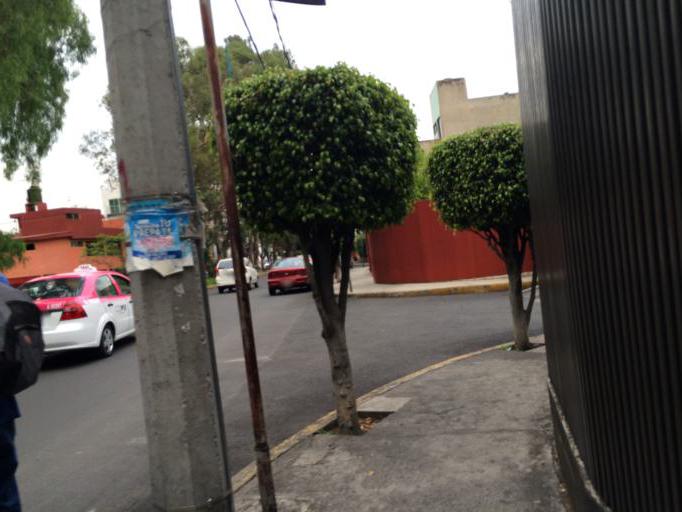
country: MX
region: Mexico City
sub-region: Iztacalco
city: Iztacalco
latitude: 19.3857
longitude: -99.0846
